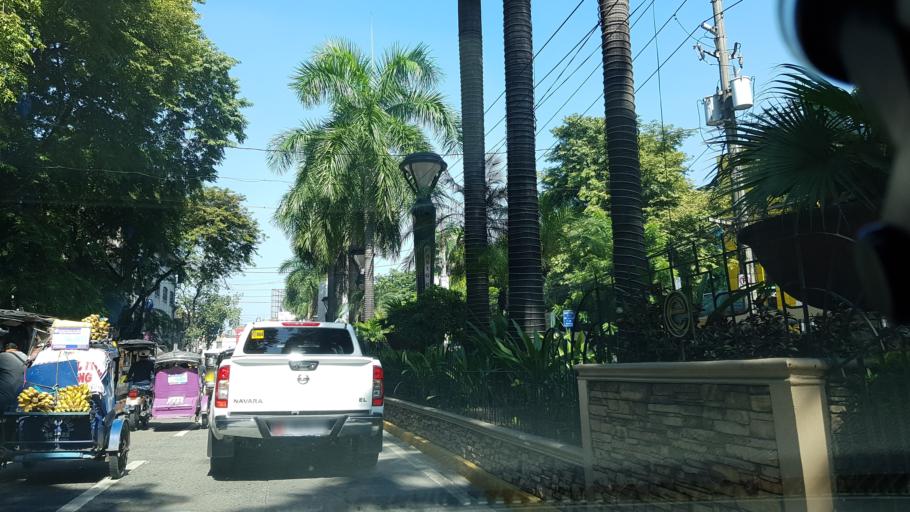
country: PH
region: Calabarzon
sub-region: Province of Rizal
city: Pateros
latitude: 14.5604
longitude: 121.0788
